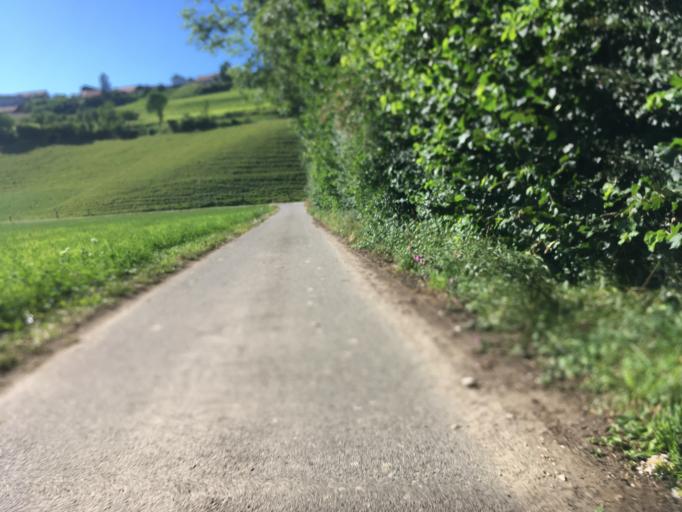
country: CH
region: Vaud
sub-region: Broye-Vully District
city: Avenches
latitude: 46.9211
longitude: 7.0295
